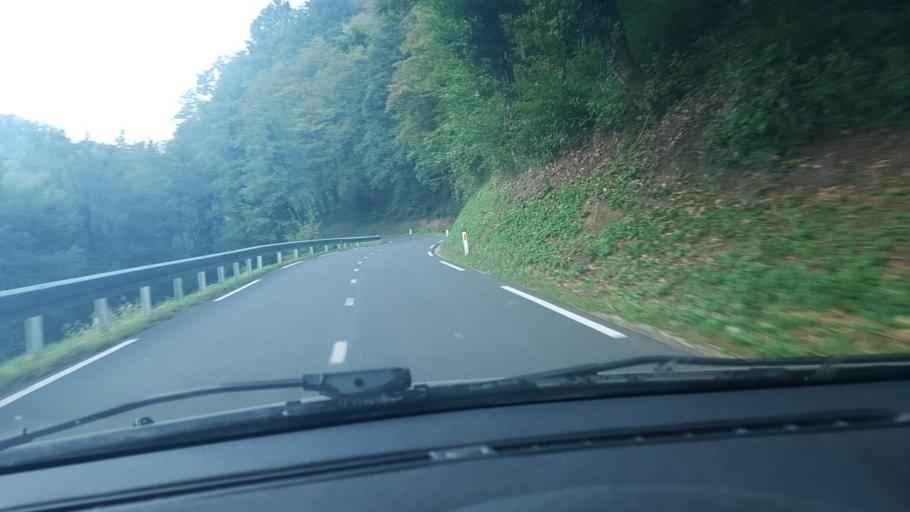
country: SI
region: Majsperk
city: Majsperk
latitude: 46.3177
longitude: 15.7186
